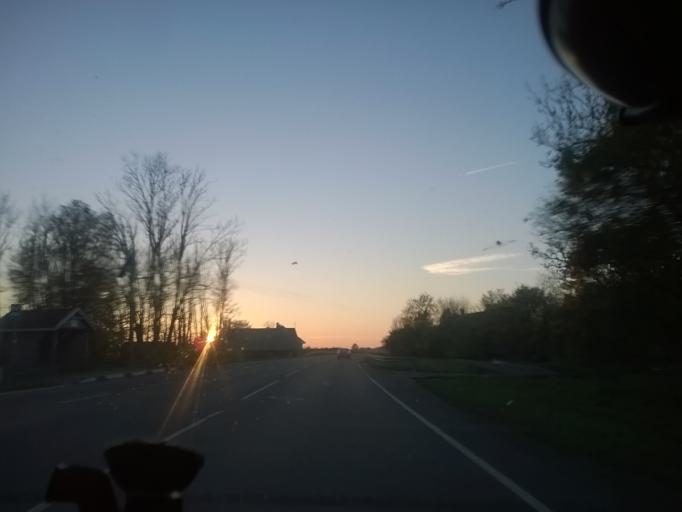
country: EE
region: Laeaene
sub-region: Ridala Parish
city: Uuemoisa
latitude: 58.9577
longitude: 23.8047
